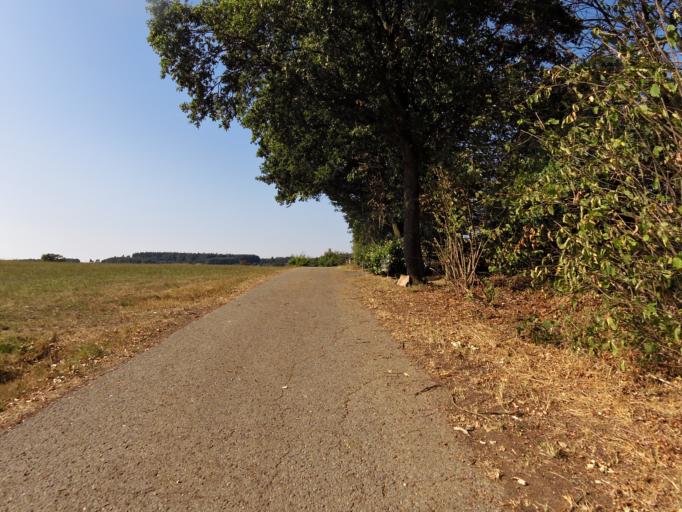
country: DE
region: Baden-Wuerttemberg
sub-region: Karlsruhe Region
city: Limbach
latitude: 49.4879
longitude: 9.2183
